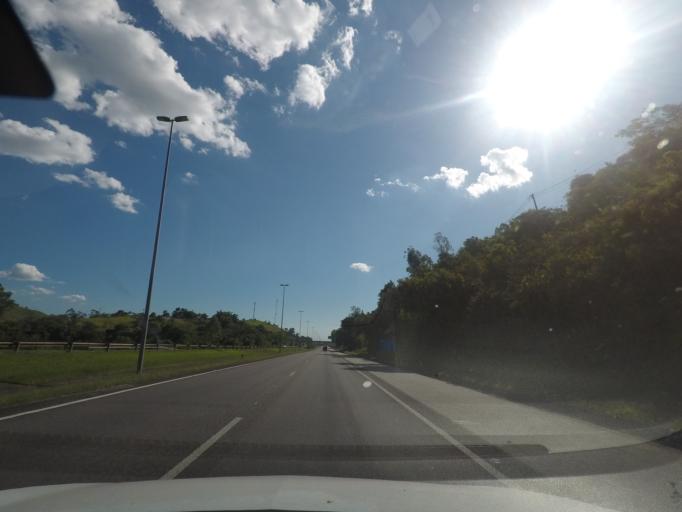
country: BR
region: Rio de Janeiro
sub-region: Guapimirim
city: Guapimirim
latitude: -22.6079
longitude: -43.0293
